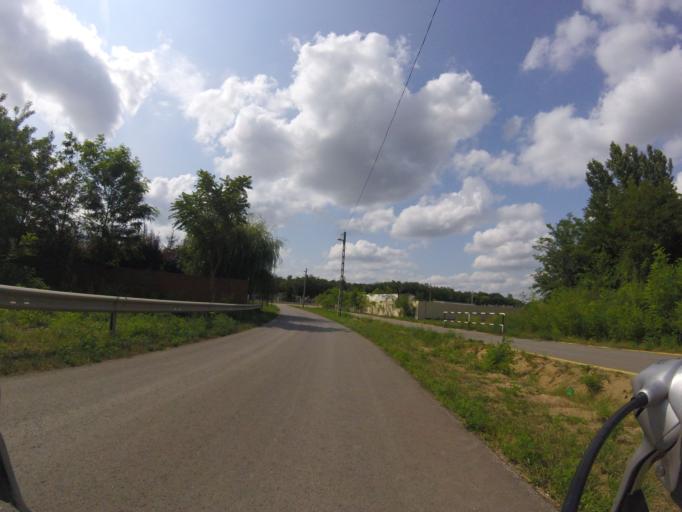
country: HU
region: Szabolcs-Szatmar-Bereg
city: Nyirpazony
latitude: 48.0105
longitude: 21.8261
